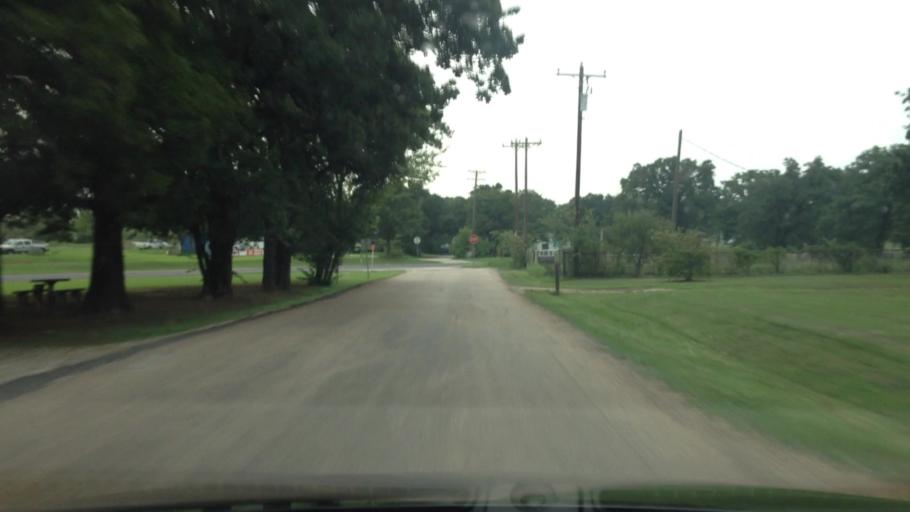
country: US
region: Texas
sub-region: Johnson County
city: Joshua
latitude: 32.4791
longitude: -97.3403
